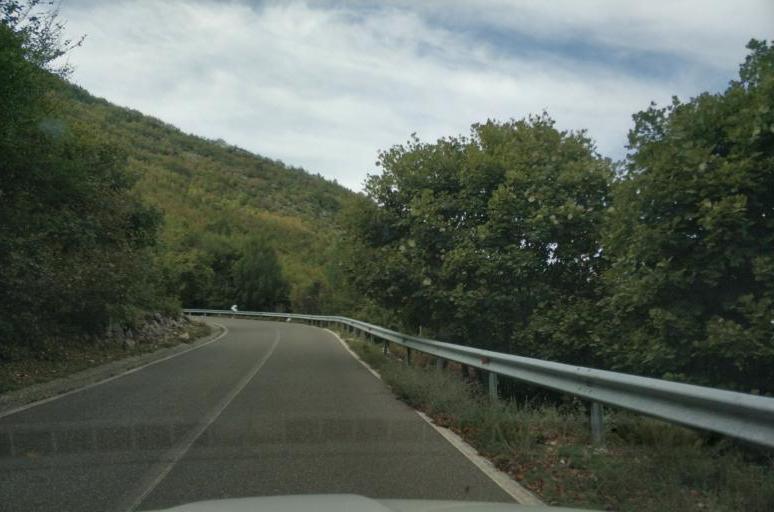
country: AL
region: Durres
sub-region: Rrethi i Krujes
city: Kruje
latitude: 41.5241
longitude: 19.8021
